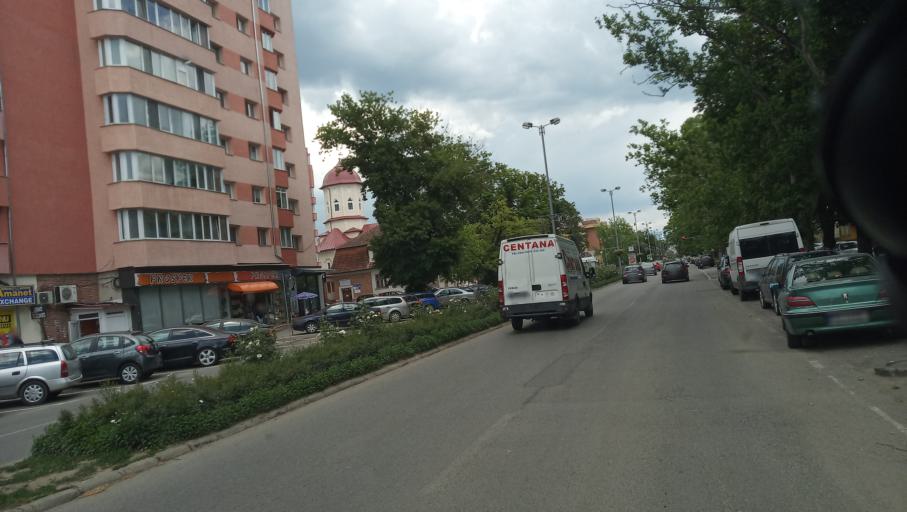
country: RO
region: Bistrita-Nasaud
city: Bistrita
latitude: 47.1263
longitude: 24.4840
